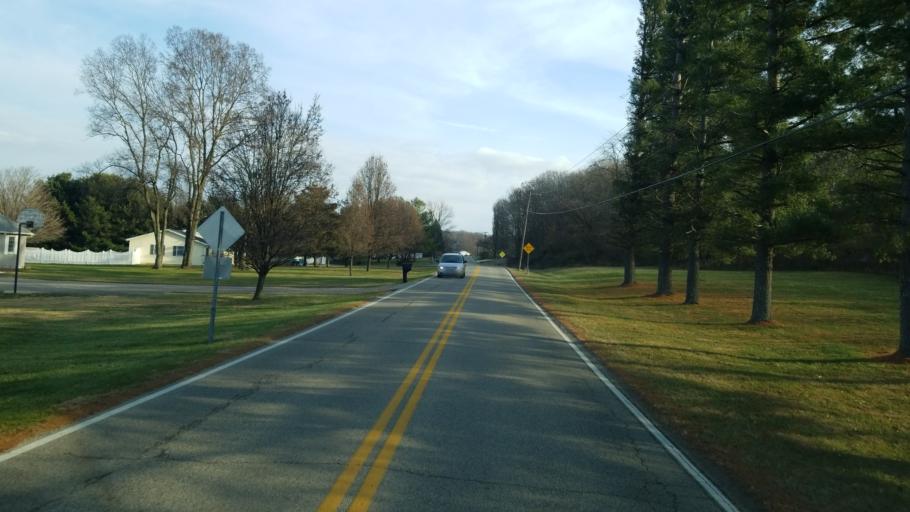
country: US
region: Ohio
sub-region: Ross County
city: Chillicothe
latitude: 39.4023
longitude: -82.9457
